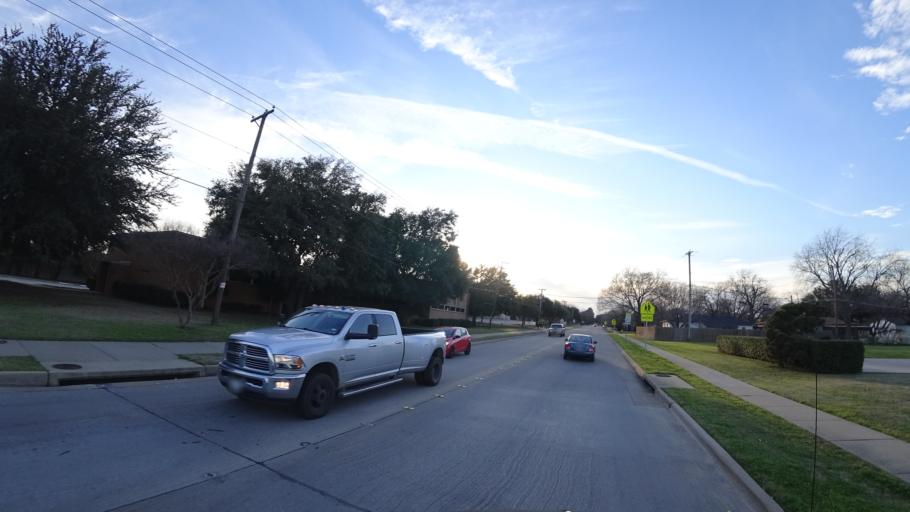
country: US
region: Texas
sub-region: Denton County
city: Lewisville
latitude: 33.0401
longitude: -96.9968
